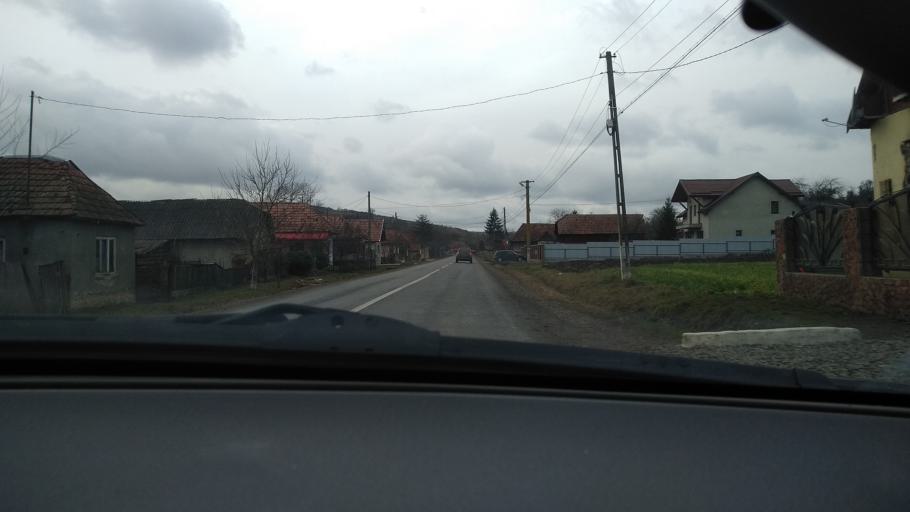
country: RO
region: Mures
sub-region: Comuna Galesti
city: Galesti
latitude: 46.5436
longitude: 24.7393
